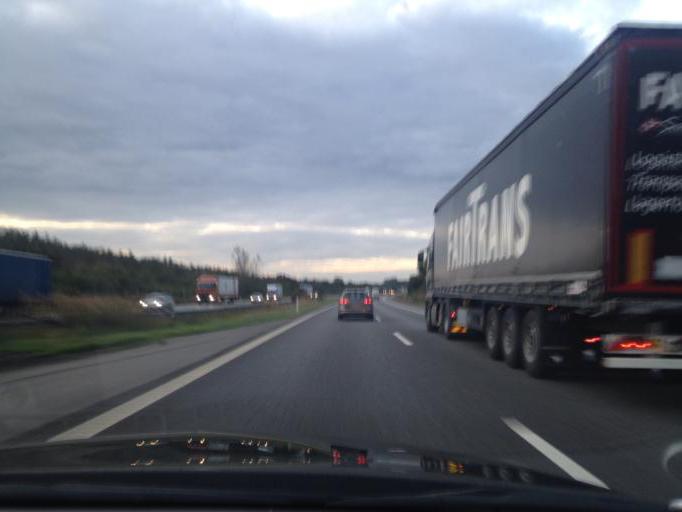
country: DK
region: South Denmark
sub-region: Kolding Kommune
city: Christiansfeld
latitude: 55.4065
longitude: 9.4539
